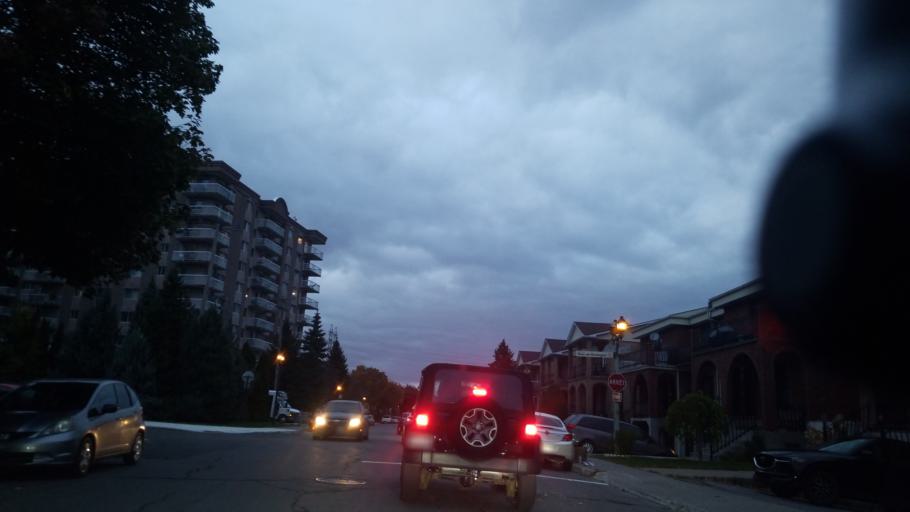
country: CA
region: Quebec
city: Mont-Royal
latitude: 45.5361
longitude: -73.6688
